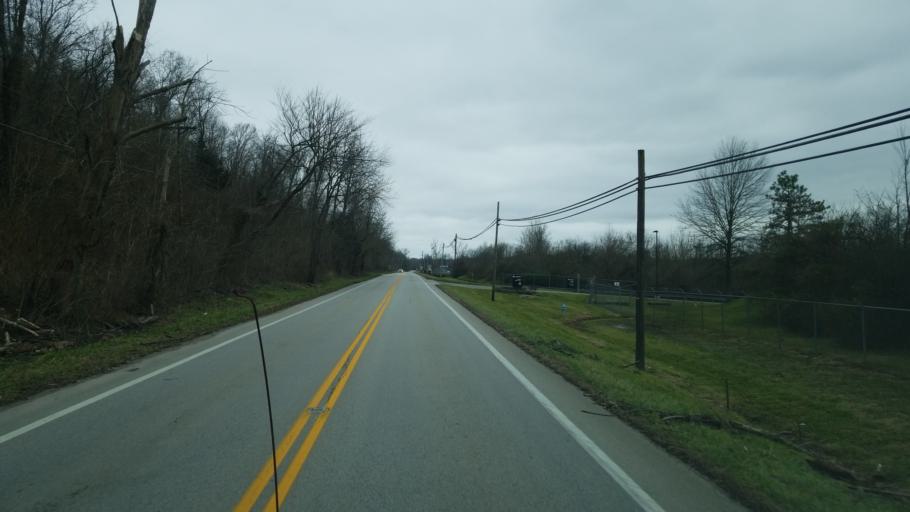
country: US
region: Ohio
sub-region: Clermont County
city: New Richmond
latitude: 38.8648
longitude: -84.2238
